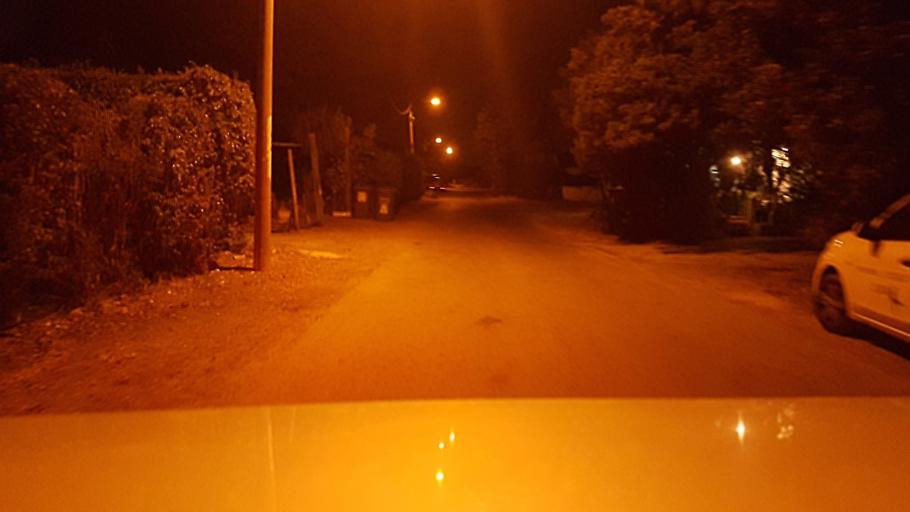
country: IL
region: Central District
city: Nehalim
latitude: 32.0793
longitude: 34.9256
